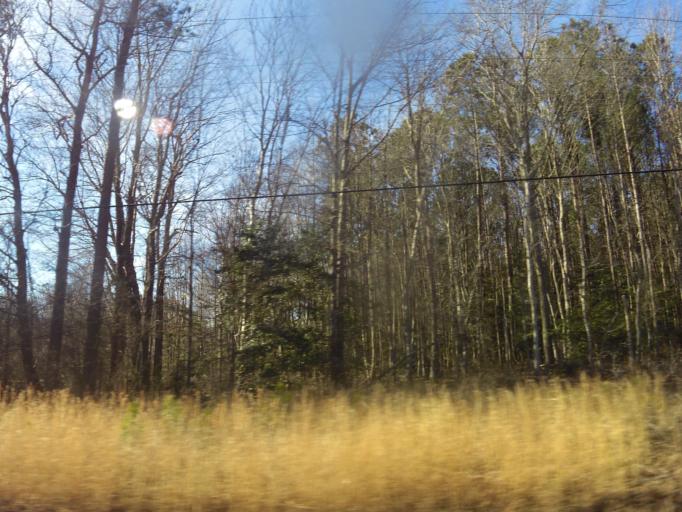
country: US
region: Virginia
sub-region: Isle of Wight County
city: Isle of Wight
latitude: 36.9311
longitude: -76.6870
